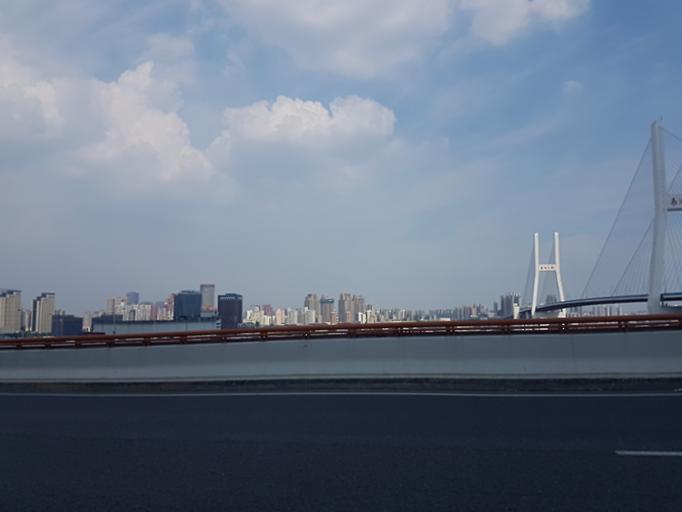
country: CN
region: Shanghai Shi
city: Luwan
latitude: 31.2105
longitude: 121.4963
